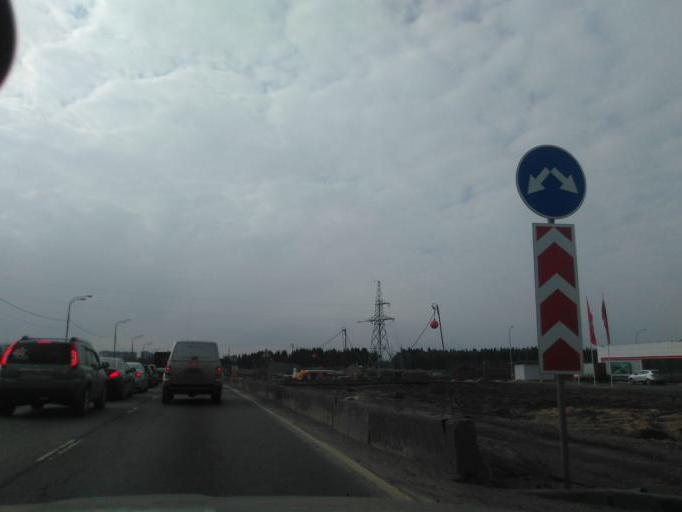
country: RU
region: Moskovskaya
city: Yermolino
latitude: 56.1443
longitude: 37.4919
